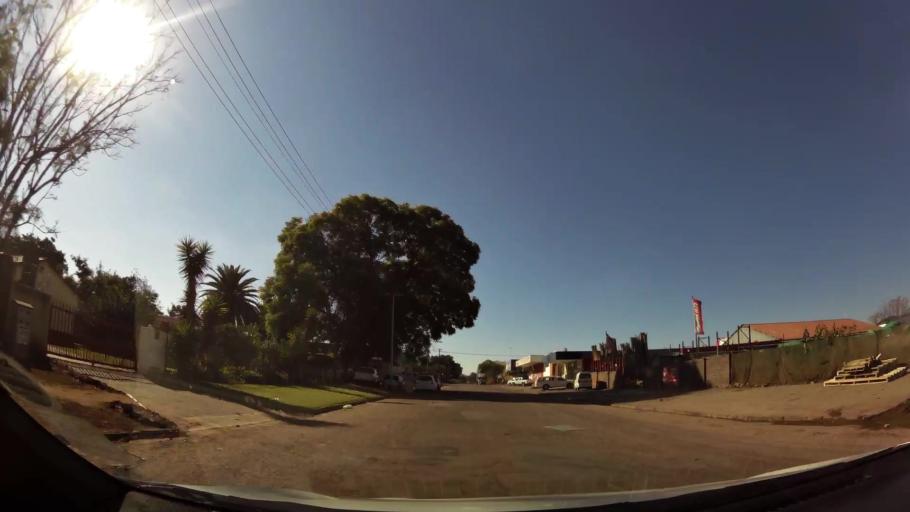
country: ZA
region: Limpopo
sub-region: Waterberg District Municipality
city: Mokopane
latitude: -24.1793
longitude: 29.0055
